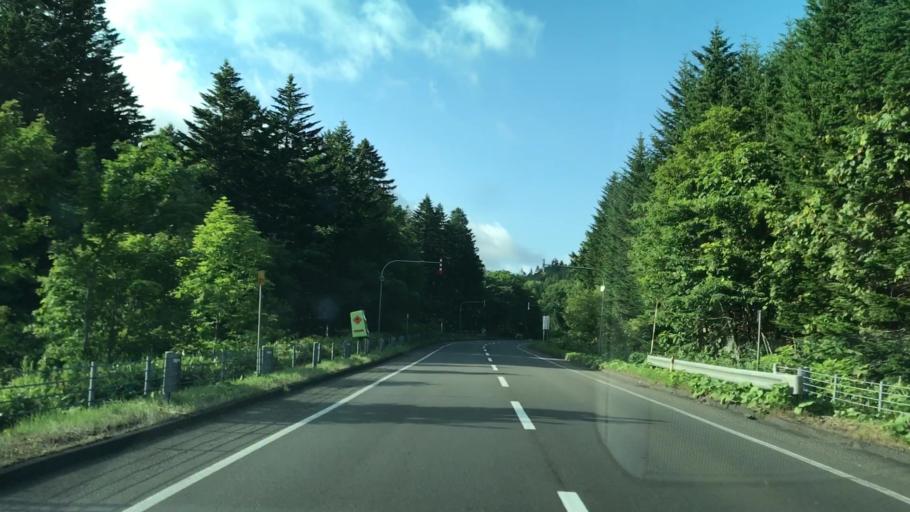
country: JP
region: Hokkaido
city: Iwamizawa
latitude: 42.9127
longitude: 142.1213
